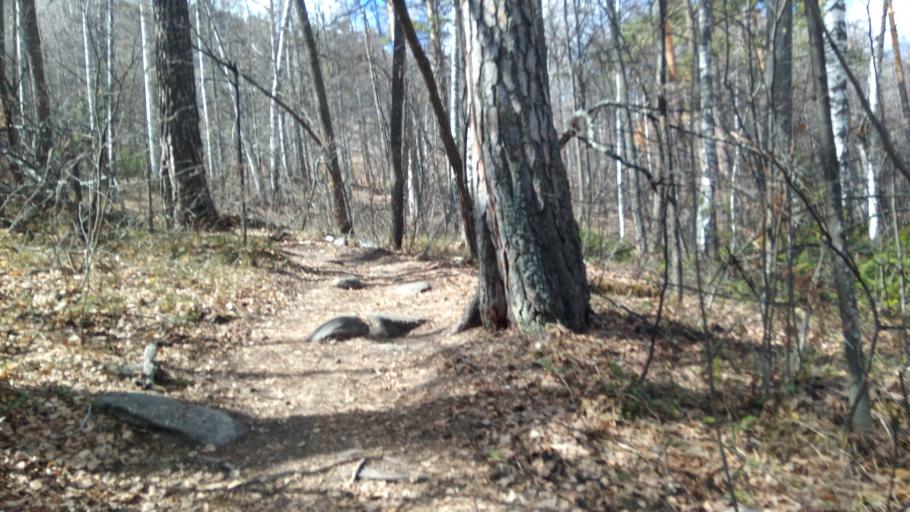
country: RU
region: Chelyabinsk
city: Syrostan
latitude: 55.1662
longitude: 59.9782
